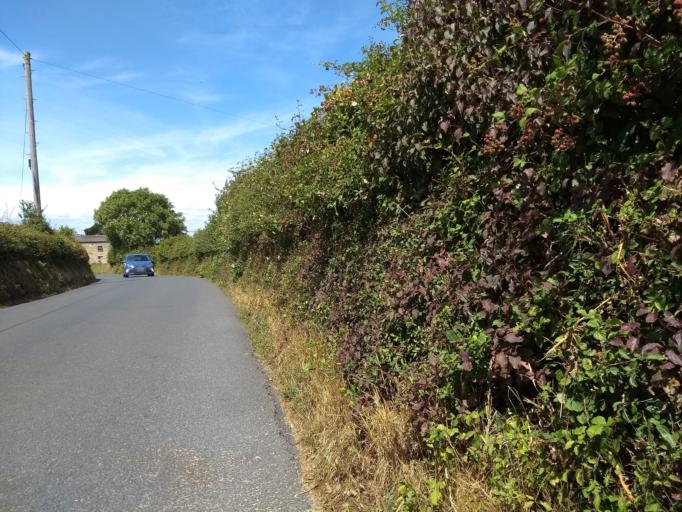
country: GB
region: England
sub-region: Isle of Wight
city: Northwood
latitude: 50.7466
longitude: -1.3157
